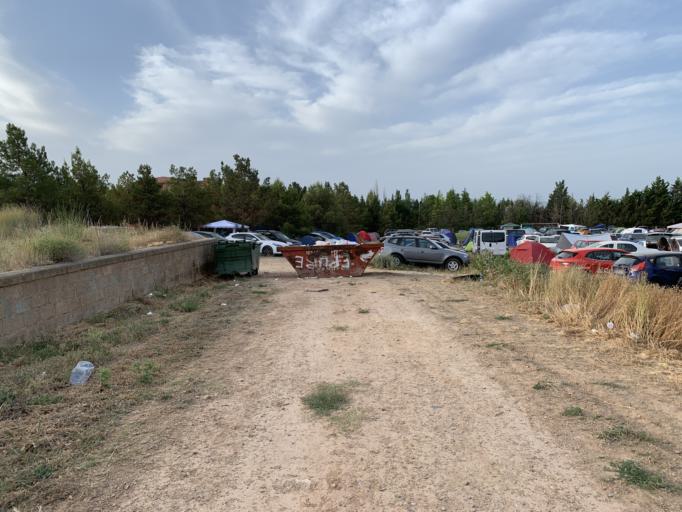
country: ES
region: Aragon
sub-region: Provincia de Teruel
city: Teruel
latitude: 40.3499
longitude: -1.1146
